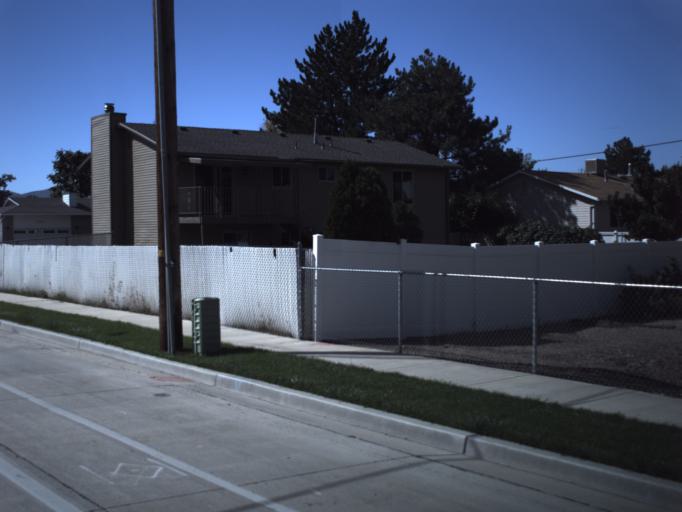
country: US
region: Utah
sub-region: Salt Lake County
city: Riverton
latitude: 40.5327
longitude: -111.9388
